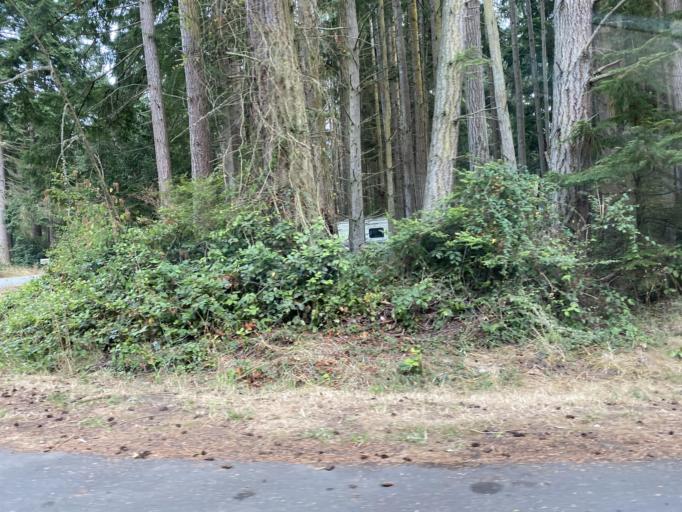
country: US
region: Washington
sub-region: Island County
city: Freeland
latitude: 48.0674
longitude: -122.5111
